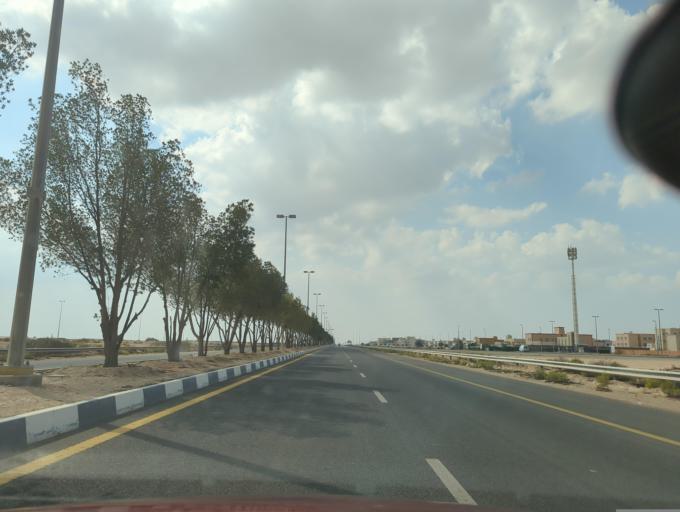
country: AE
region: Abu Dhabi
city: Abu Dhabi
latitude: 24.3656
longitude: 54.7208
